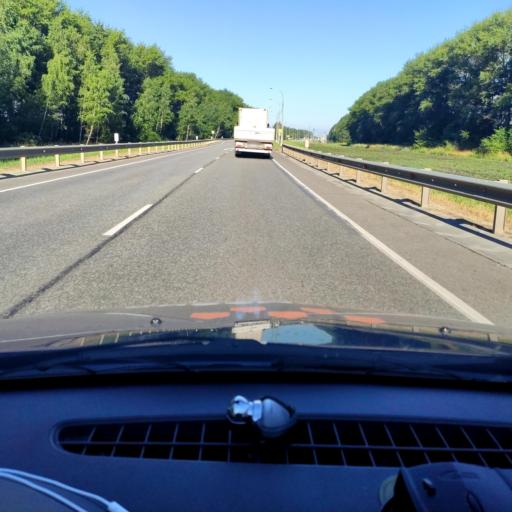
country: RU
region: Orjol
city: Zmiyevka
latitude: 52.6353
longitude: 36.6198
